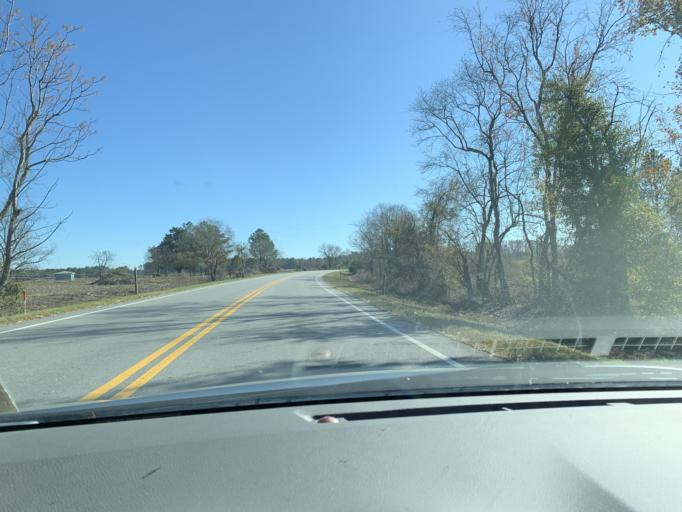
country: US
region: Georgia
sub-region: Ben Hill County
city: Fitzgerald
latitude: 31.7146
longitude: -83.1758
